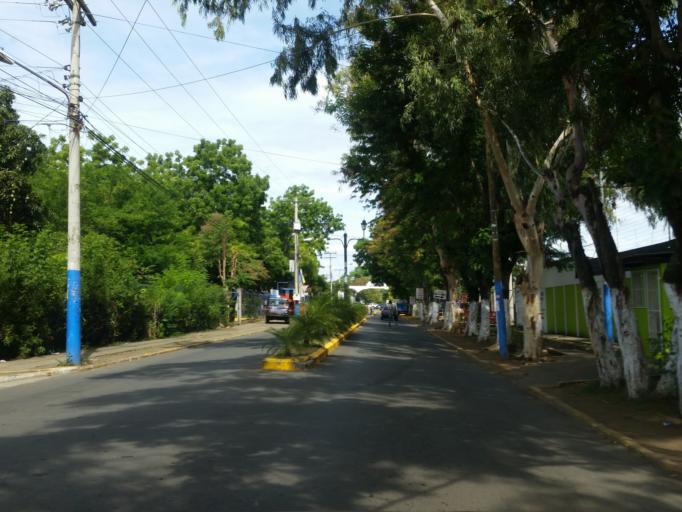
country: NI
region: Masaya
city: Nindiri
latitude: 12.0009
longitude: -86.1175
